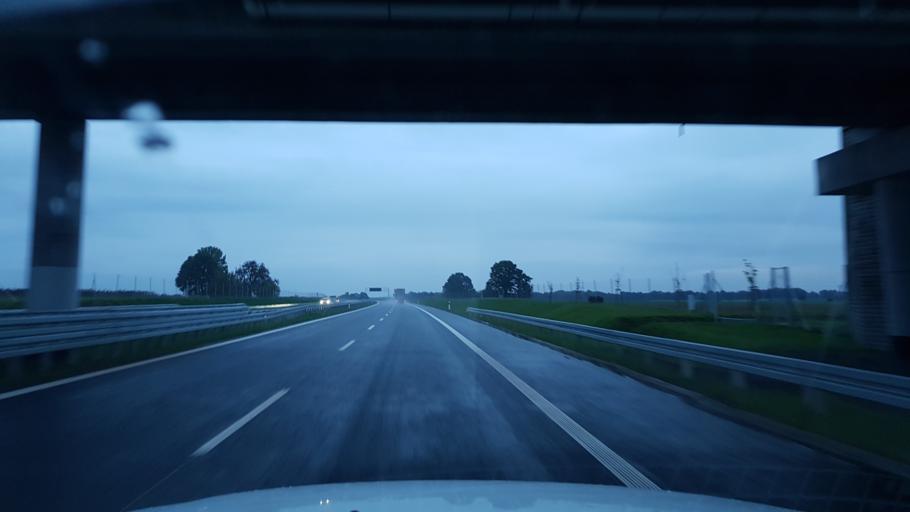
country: PL
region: West Pomeranian Voivodeship
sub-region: Powiat gryficki
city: Brojce
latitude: 53.8835
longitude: 15.3789
